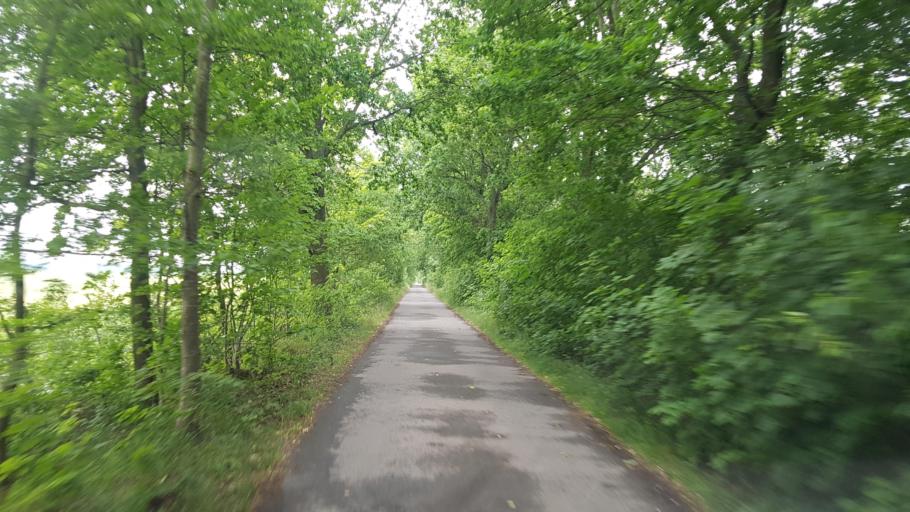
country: DE
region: Brandenburg
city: Grossthiemig
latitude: 51.4017
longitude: 13.6490
